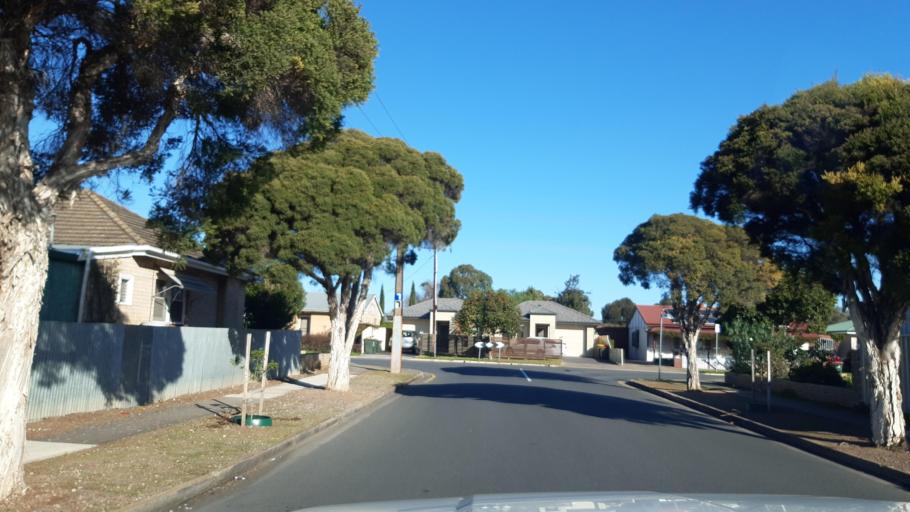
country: AU
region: South Australia
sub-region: Marion
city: Clovelly Park
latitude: -34.9970
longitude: 138.5674
